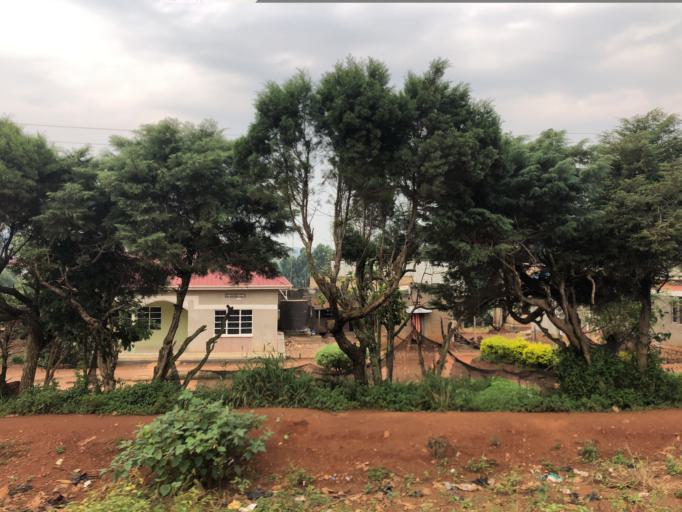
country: UG
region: Central Region
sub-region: Mukono District
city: Mukono
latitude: 0.3475
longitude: 32.7633
